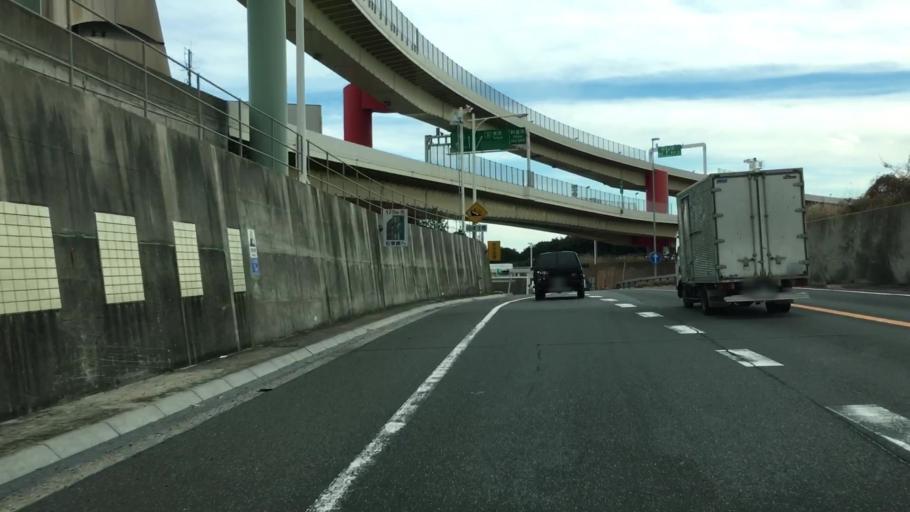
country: JP
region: Kanagawa
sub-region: Kawasaki-shi
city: Kawasaki
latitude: 35.5194
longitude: 139.7906
